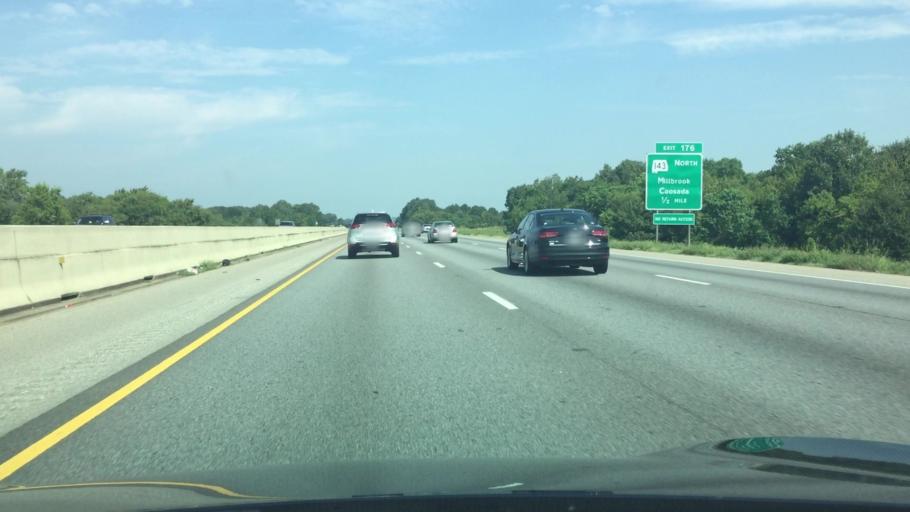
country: US
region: Alabama
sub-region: Montgomery County
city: Montgomery
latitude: 32.4089
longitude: -86.3462
